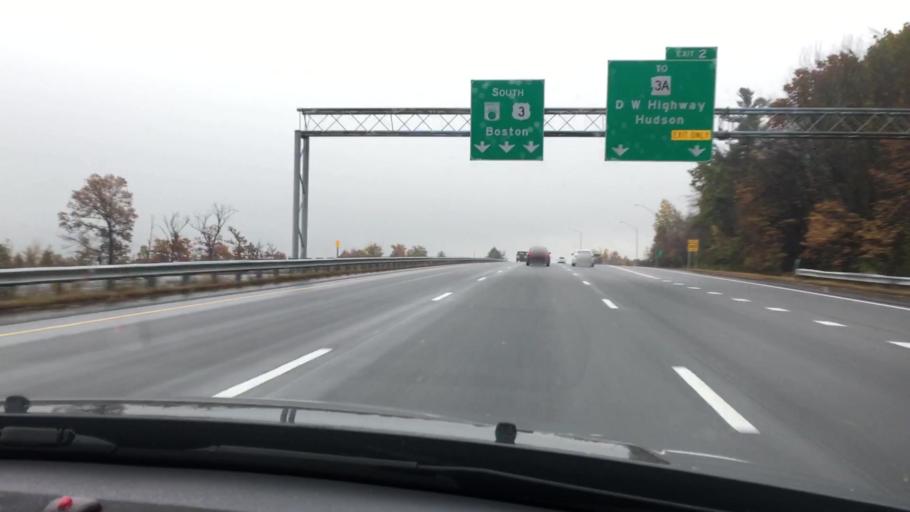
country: US
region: New Hampshire
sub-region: Hillsborough County
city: Hudson
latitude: 42.7305
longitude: -71.4531
